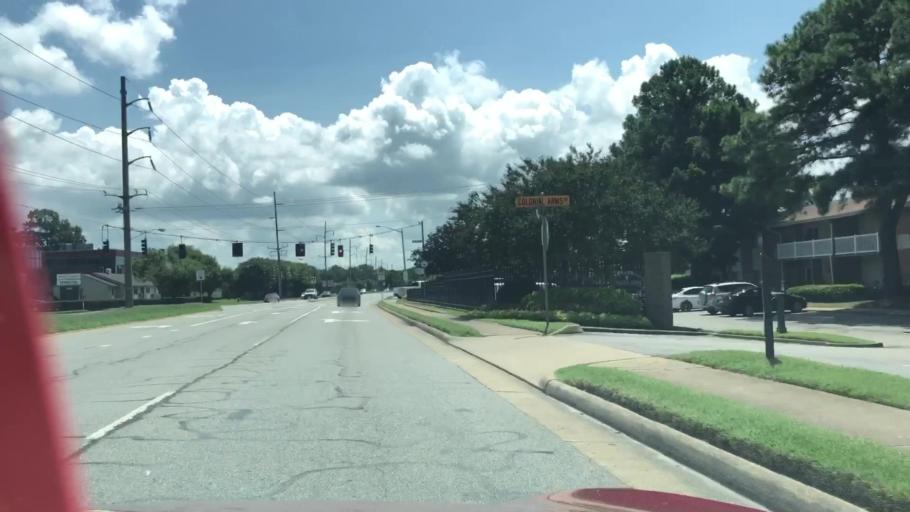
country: US
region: Virginia
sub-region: City of Virginia Beach
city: Virginia Beach
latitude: 36.8619
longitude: -76.0275
